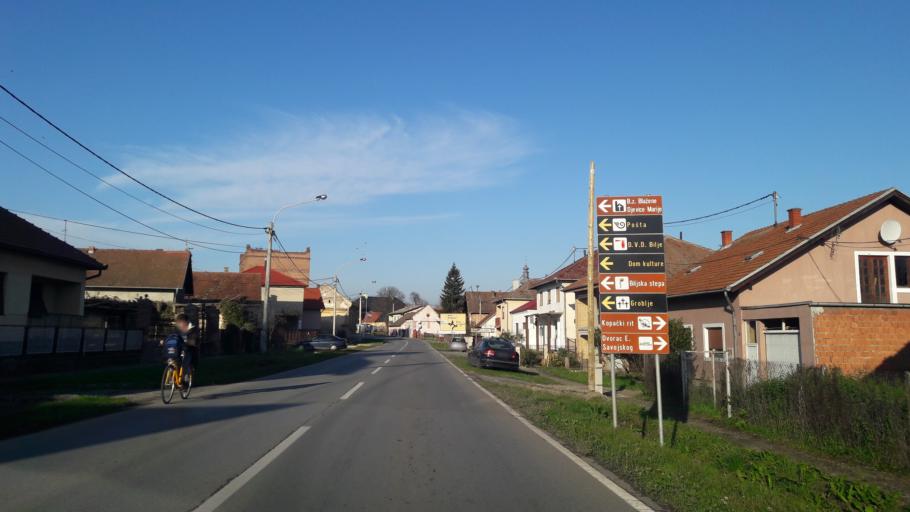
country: HR
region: Osjecko-Baranjska
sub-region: Grad Osijek
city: Bilje
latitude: 45.6011
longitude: 18.7436
